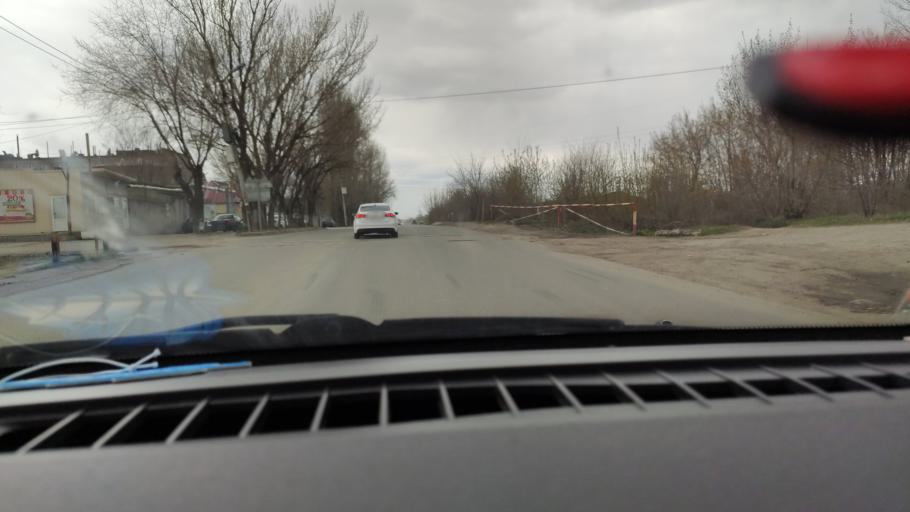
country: RU
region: Saratov
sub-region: Saratovskiy Rayon
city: Saratov
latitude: 51.6150
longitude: 45.9565
